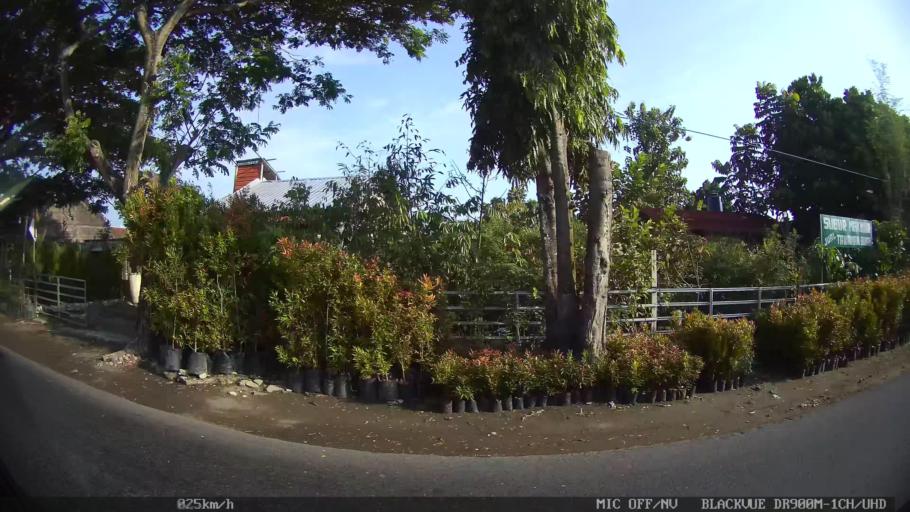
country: ID
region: Daerah Istimewa Yogyakarta
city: Sewon
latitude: -7.8677
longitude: 110.3495
